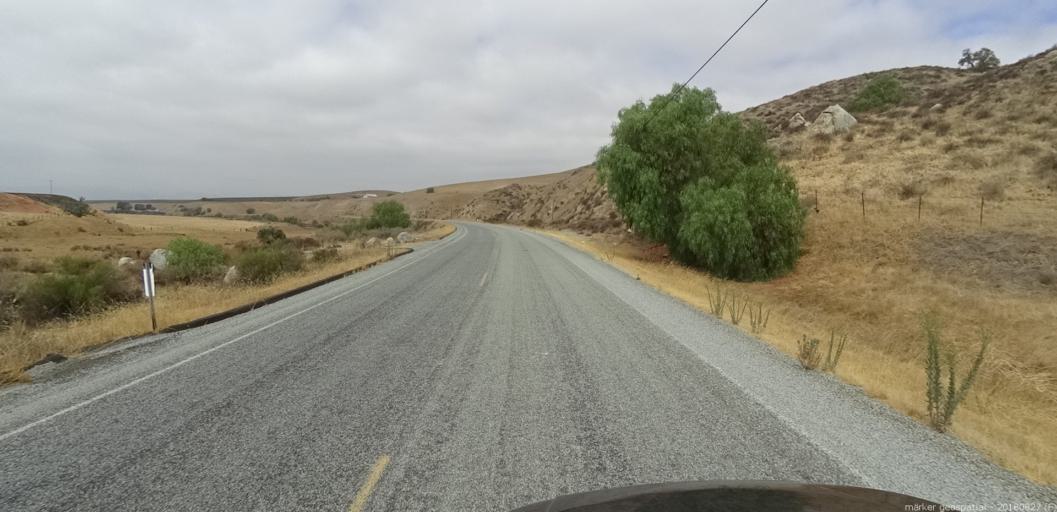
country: US
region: California
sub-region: Monterey County
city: King City
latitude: 36.2680
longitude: -121.0719
